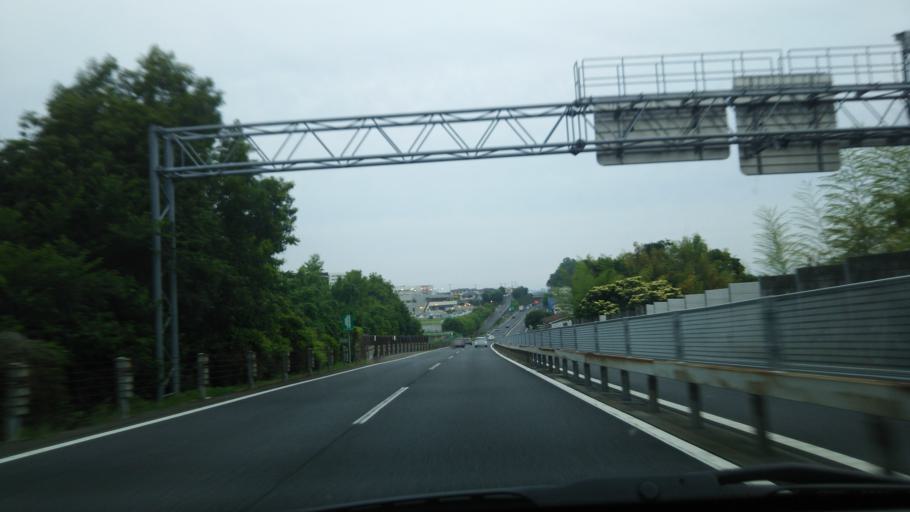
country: JP
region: Kanagawa
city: Oiso
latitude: 35.3456
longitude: 139.2969
